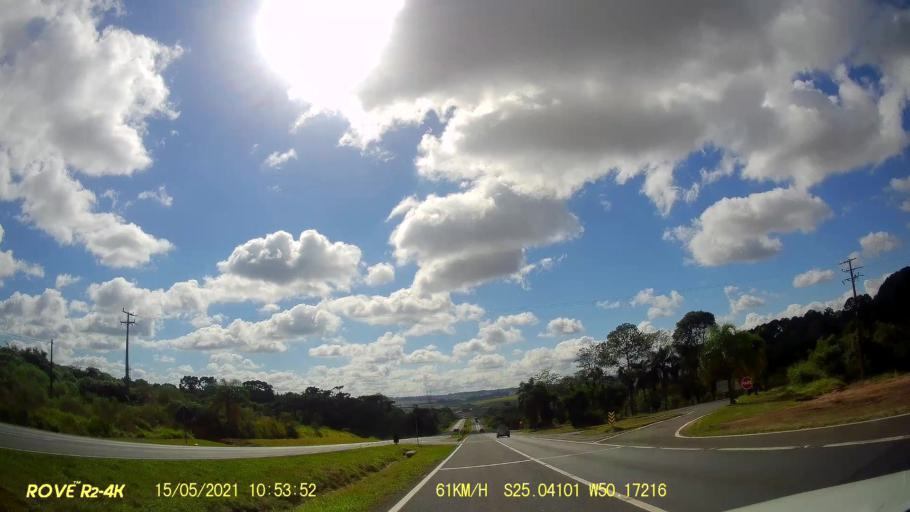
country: BR
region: Parana
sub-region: Ponta Grossa
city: Ponta Grossa
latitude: -25.0417
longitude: -50.1718
